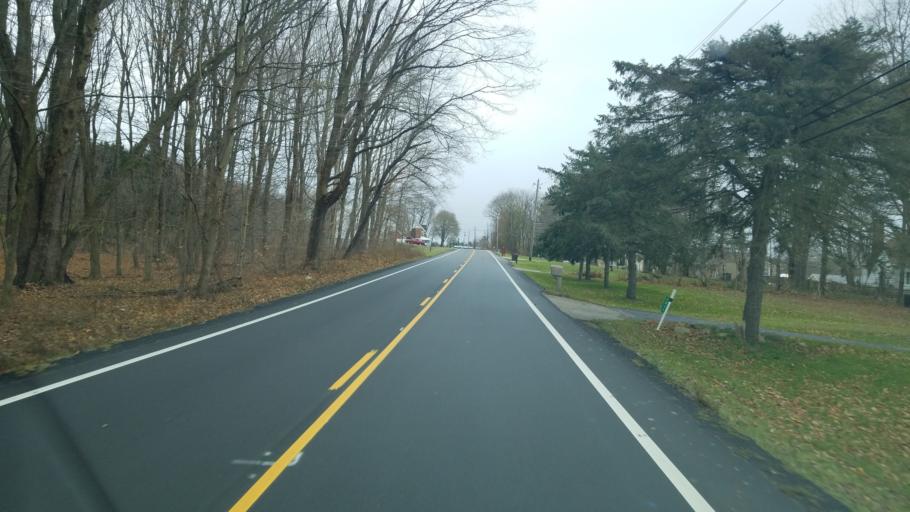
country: US
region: Ohio
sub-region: Ashtabula County
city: Edgewood
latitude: 41.8663
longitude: -80.7553
